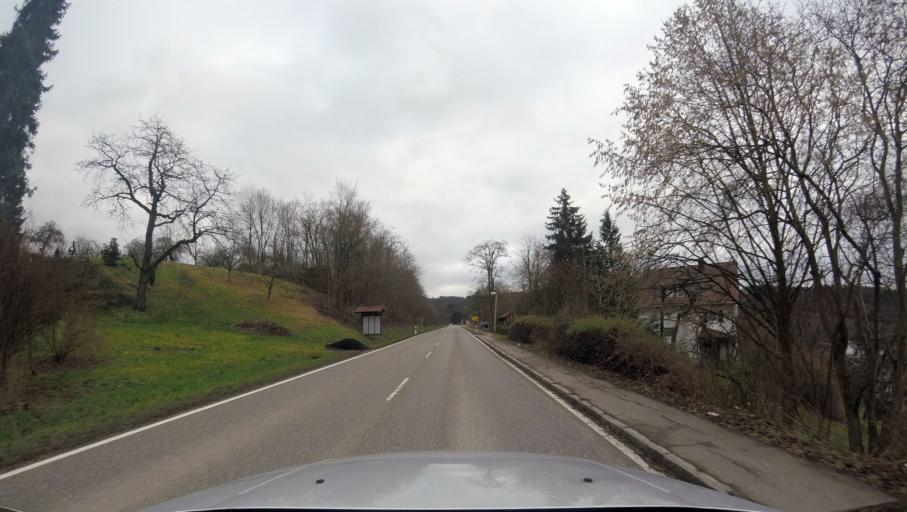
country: DE
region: Baden-Wuerttemberg
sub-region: Regierungsbezirk Stuttgart
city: Allmersbach im Tal
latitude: 48.9046
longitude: 9.4736
